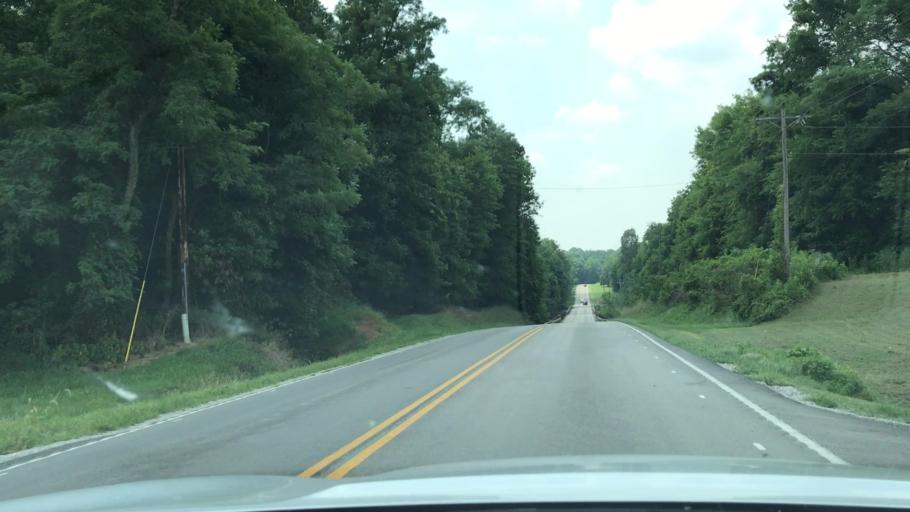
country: US
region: Kentucky
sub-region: Todd County
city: Guthrie
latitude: 36.7141
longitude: -87.0978
